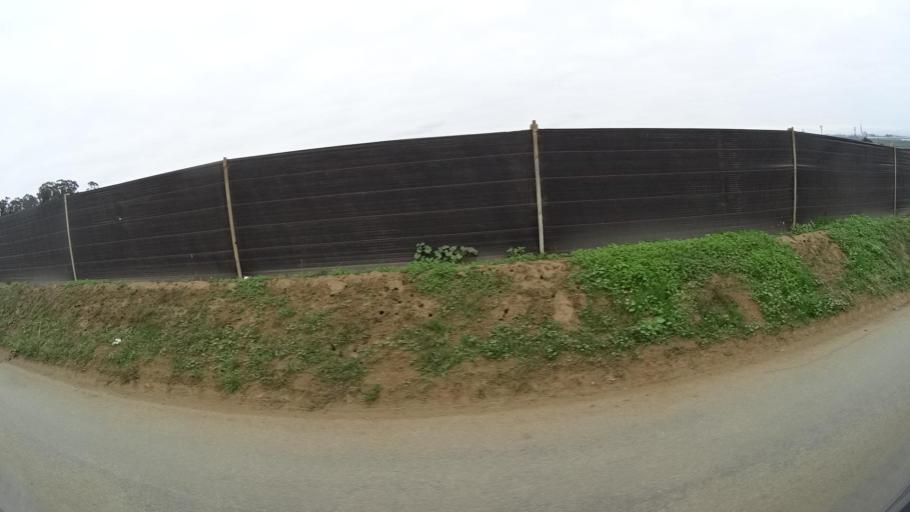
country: US
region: California
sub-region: Monterey County
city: Las Lomas
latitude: 36.8572
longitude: -121.7954
